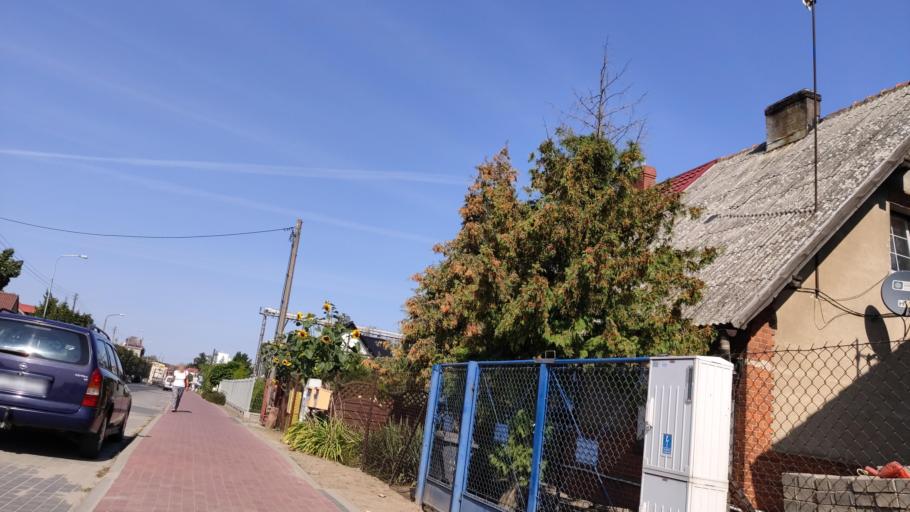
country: PL
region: Kujawsko-Pomorskie
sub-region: Powiat zninski
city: Znin
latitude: 52.8448
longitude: 17.7429
